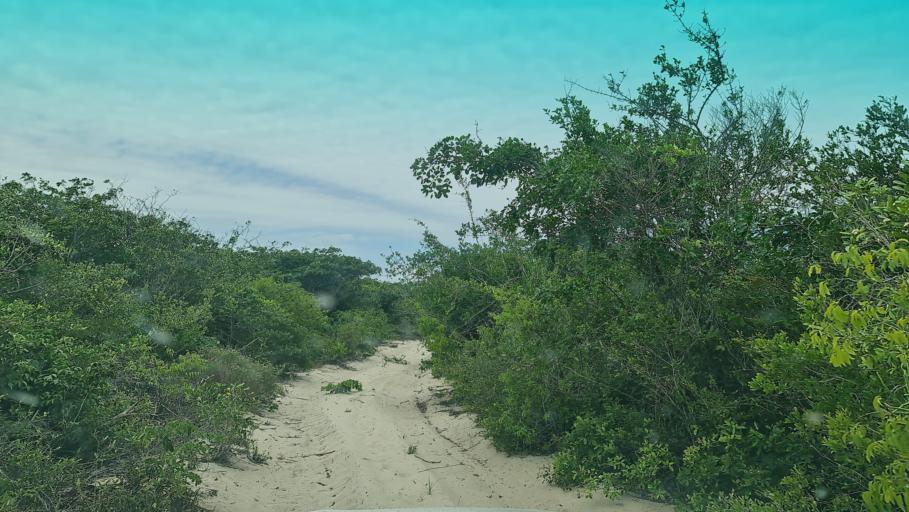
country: MZ
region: Maputo
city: Manhica
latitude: -25.6351
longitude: 32.7854
